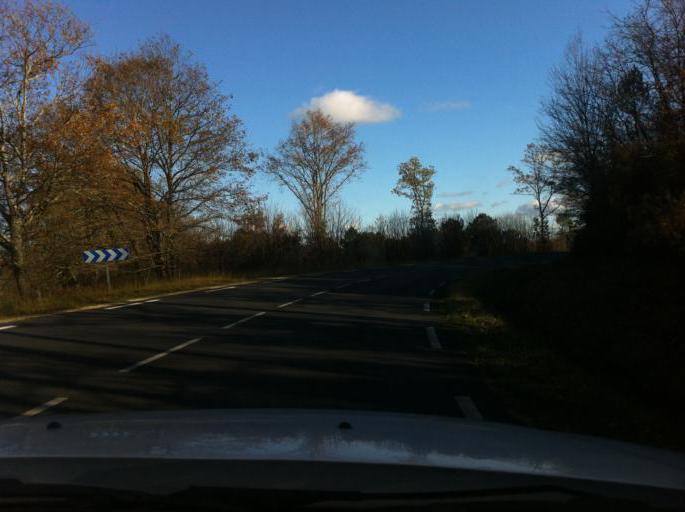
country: FR
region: Aquitaine
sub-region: Departement de la Dordogne
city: Rouffignac-Saint-Cernin-de-Reilhac
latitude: 45.0405
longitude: 0.8678
